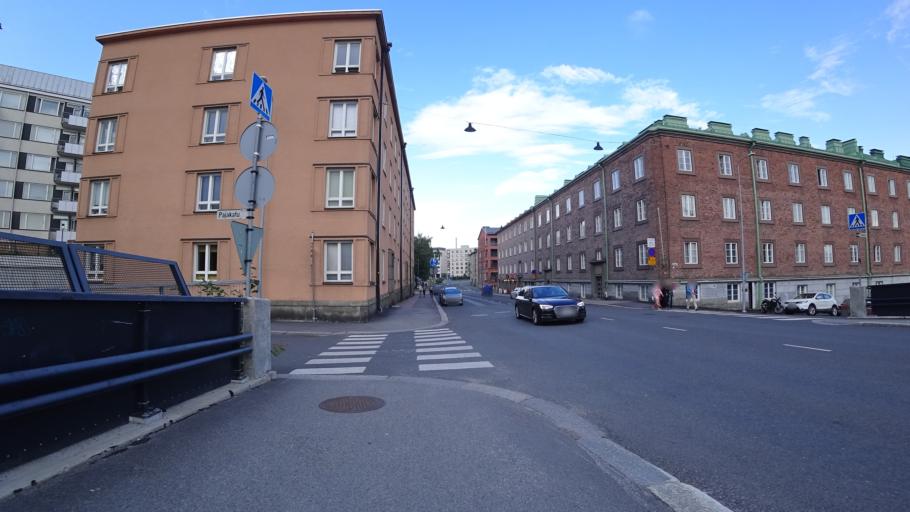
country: FI
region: Pirkanmaa
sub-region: Tampere
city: Tampere
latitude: 61.5049
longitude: 23.7700
